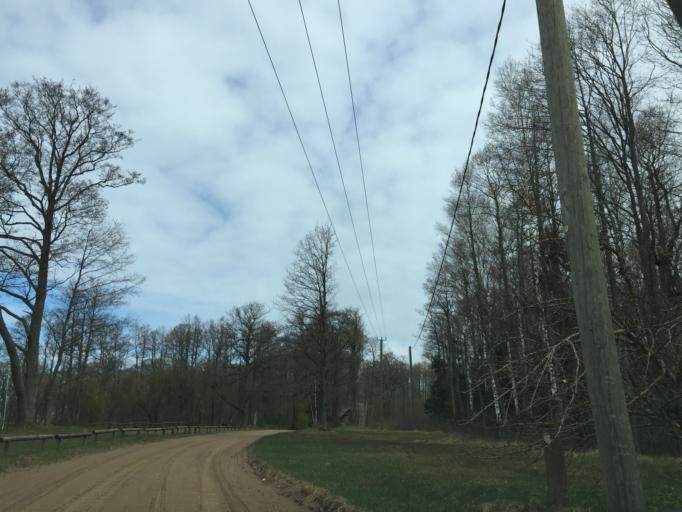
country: LV
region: Salacgrivas
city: Salacgriva
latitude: 57.5199
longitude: 24.3794
